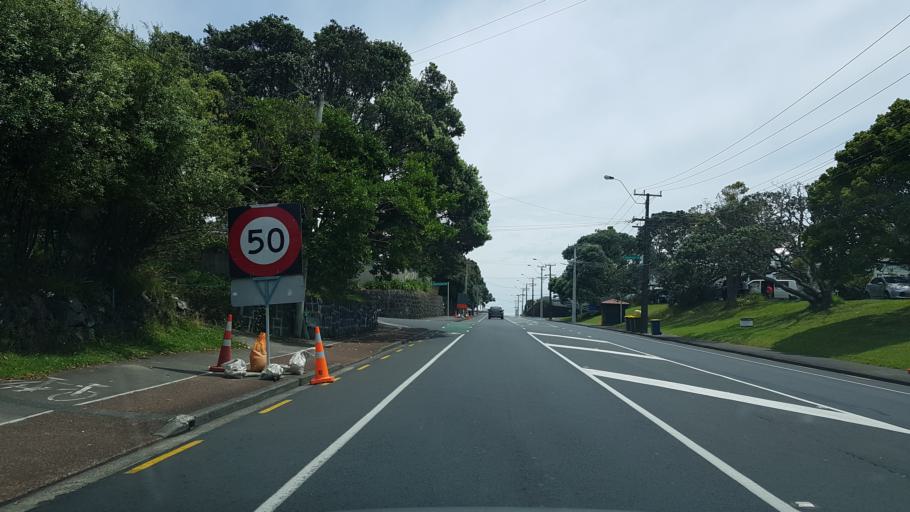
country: NZ
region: Auckland
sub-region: Auckland
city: North Shore
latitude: -36.8164
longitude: 174.7939
